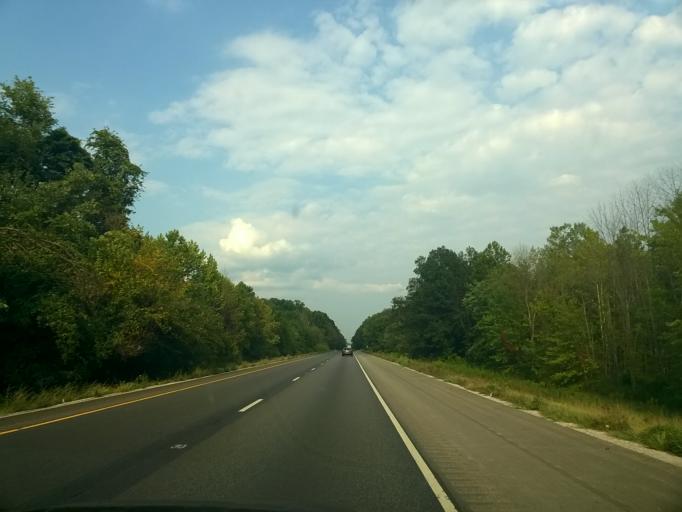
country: US
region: Indiana
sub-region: Clay County
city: Brazil
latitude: 39.4528
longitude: -87.1025
